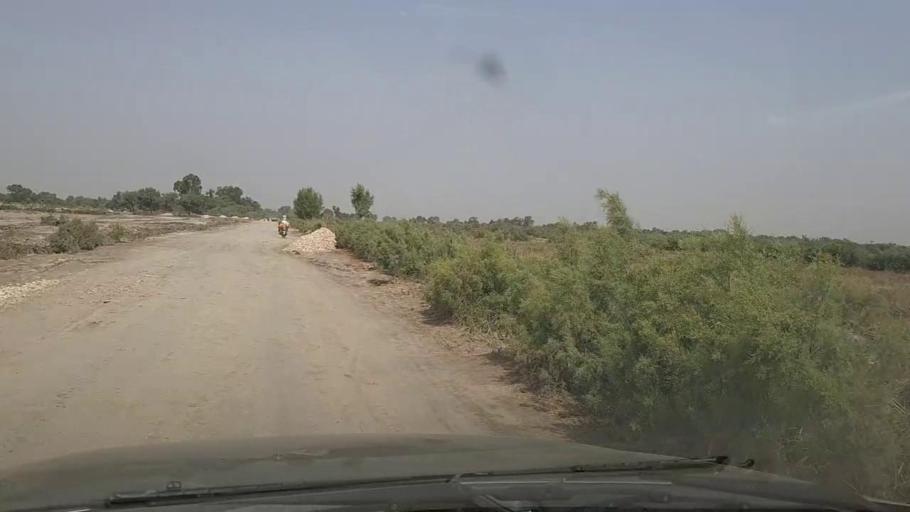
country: PK
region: Sindh
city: Thul
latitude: 28.3985
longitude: 68.7106
